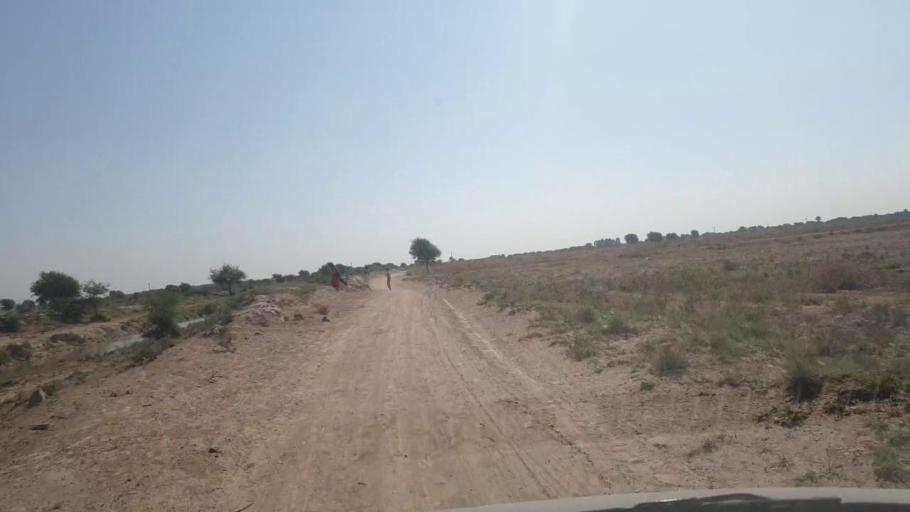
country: PK
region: Sindh
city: Digri
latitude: 24.9371
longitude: 69.1622
